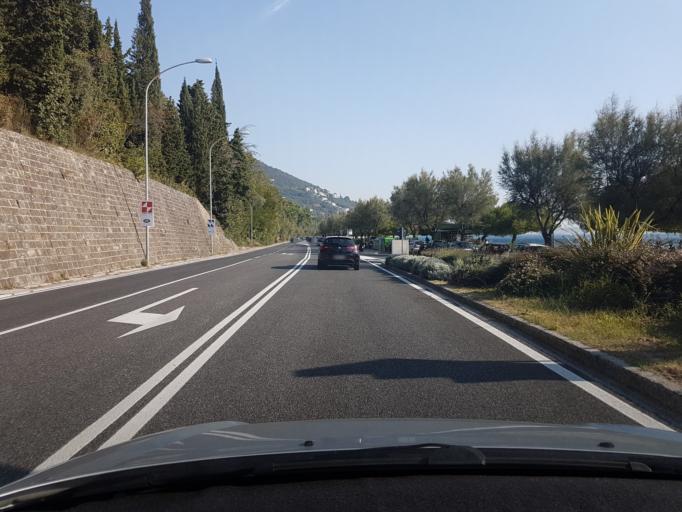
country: IT
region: Friuli Venezia Giulia
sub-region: Provincia di Trieste
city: Prosecco-Contovello
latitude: 45.6991
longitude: 13.7267
